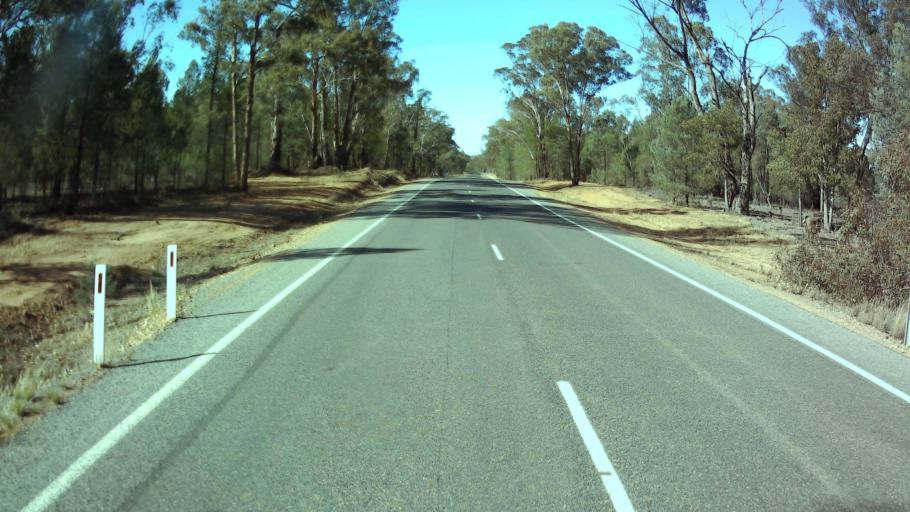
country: AU
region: New South Wales
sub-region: Weddin
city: Grenfell
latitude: -33.7508
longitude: 148.0850
